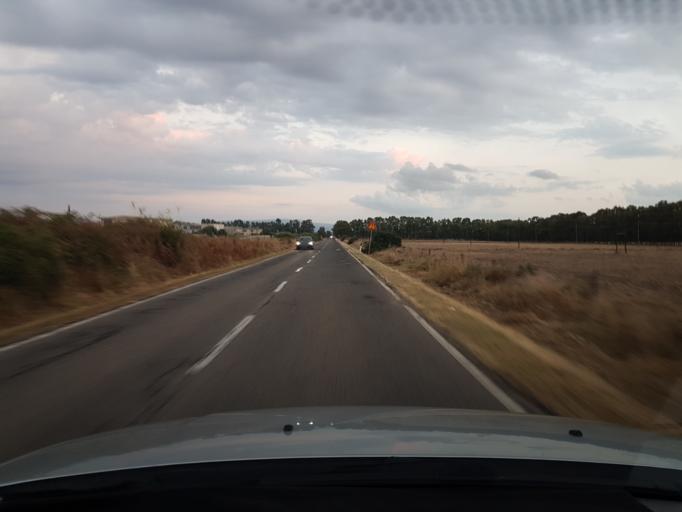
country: IT
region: Sardinia
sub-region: Provincia di Oristano
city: Milis
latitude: 40.0384
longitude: 8.6370
